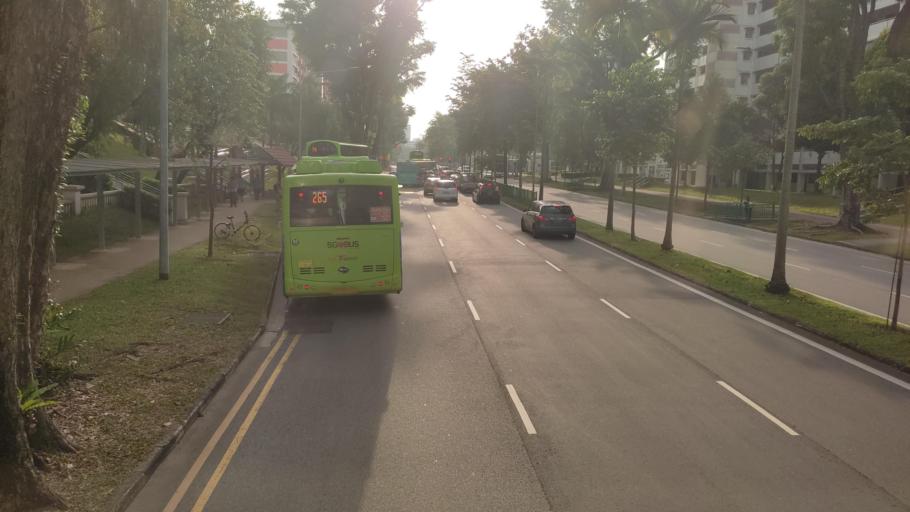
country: SG
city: Singapore
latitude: 1.3697
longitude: 103.8415
